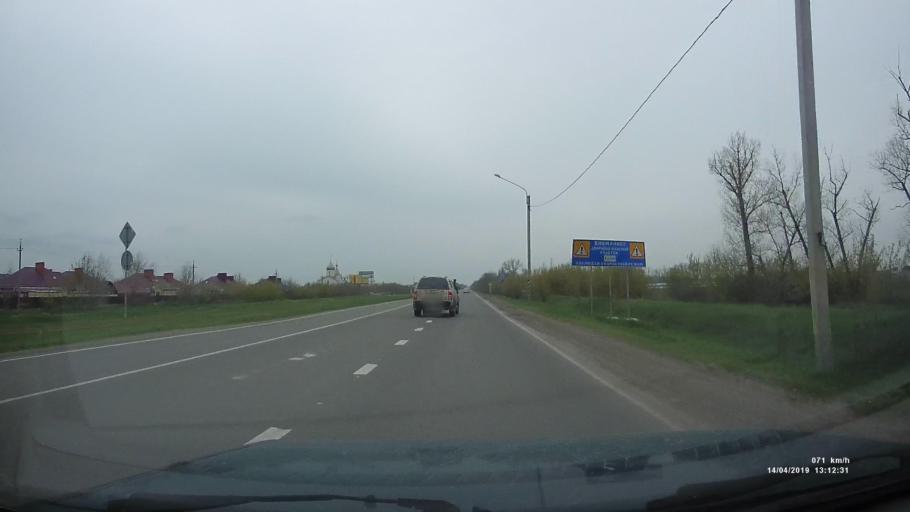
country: RU
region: Rostov
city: Kuleshovka
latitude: 47.1025
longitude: 39.6369
